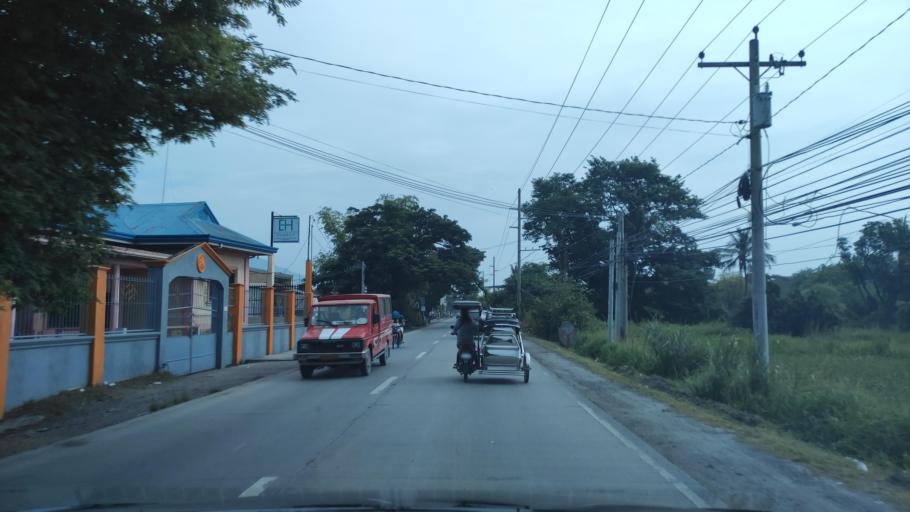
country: PH
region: Central Luzon
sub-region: Province of Pampanga
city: Arayat
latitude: 15.1227
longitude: 120.7761
